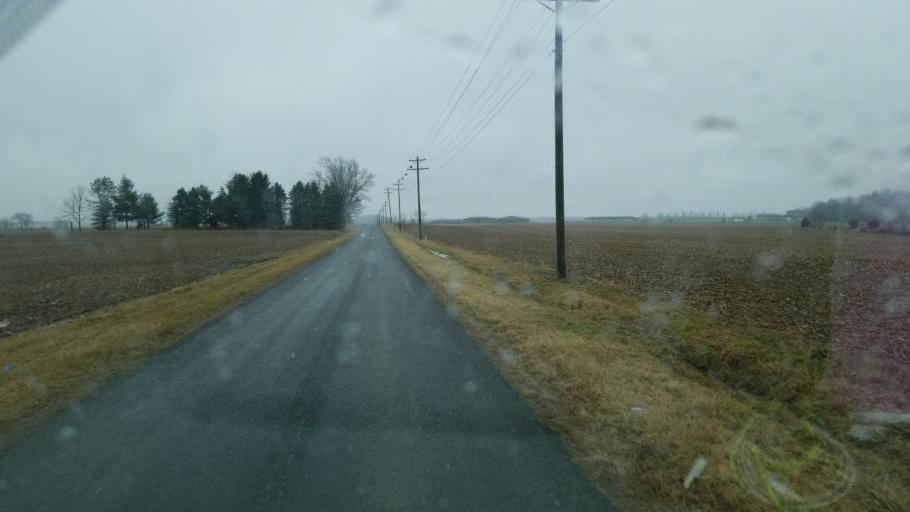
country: US
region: Ohio
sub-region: Union County
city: New California
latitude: 40.2029
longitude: -83.2673
